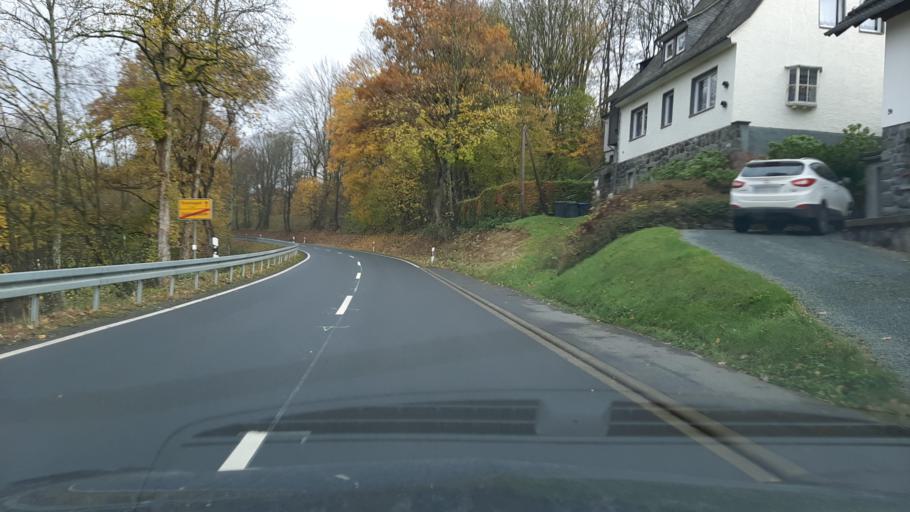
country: DE
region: North Rhine-Westphalia
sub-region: Regierungsbezirk Arnsberg
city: Winterberg
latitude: 51.2568
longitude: 8.4722
